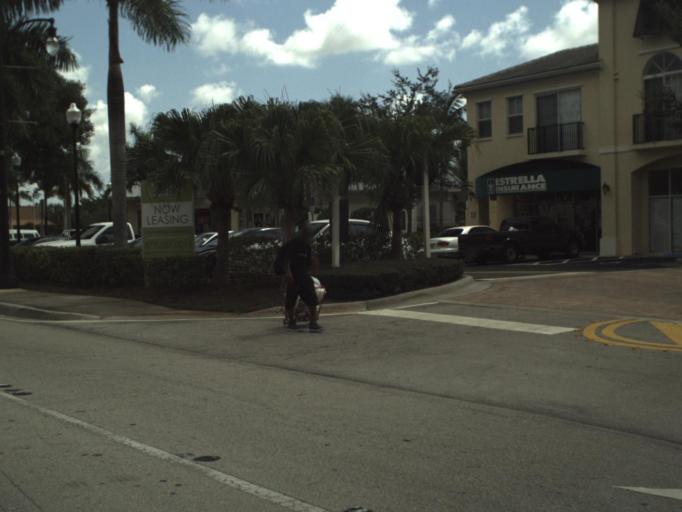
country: US
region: Florida
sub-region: Broward County
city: Broward Estates
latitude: 26.1200
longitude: -80.2018
